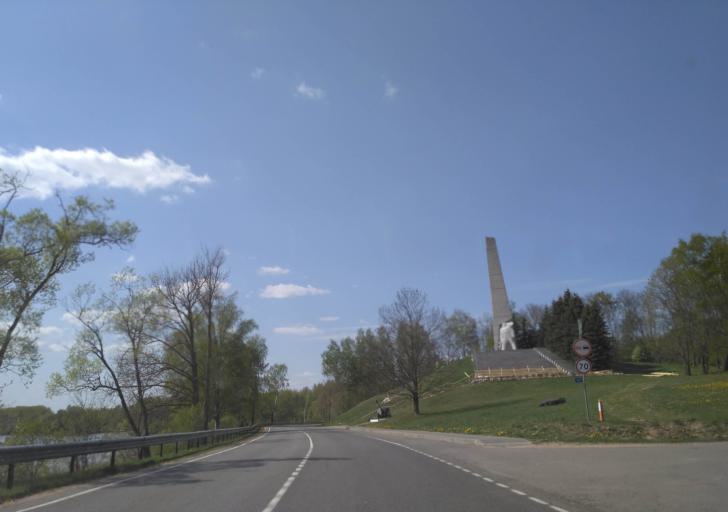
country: BY
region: Minsk
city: Myadzyel
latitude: 54.8849
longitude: 26.8382
